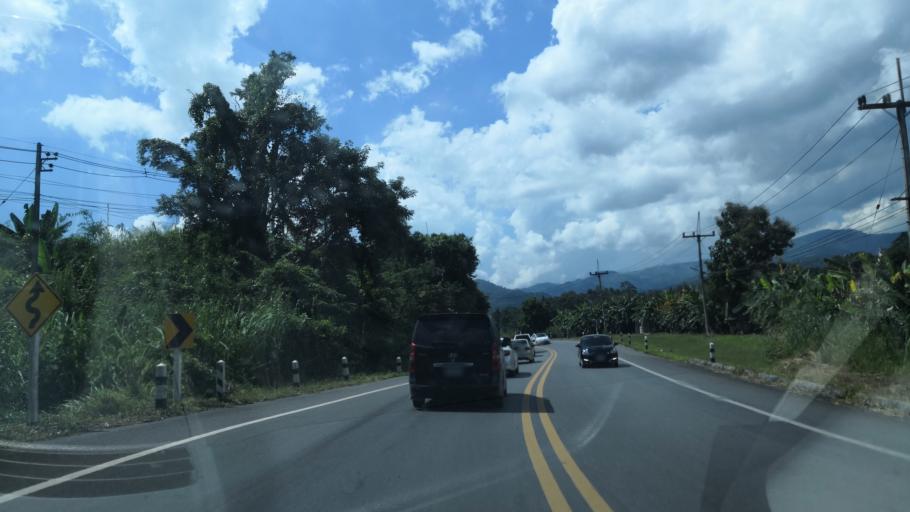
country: TH
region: Chiang Rai
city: Mae Lao
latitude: 19.7361
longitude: 99.6348
